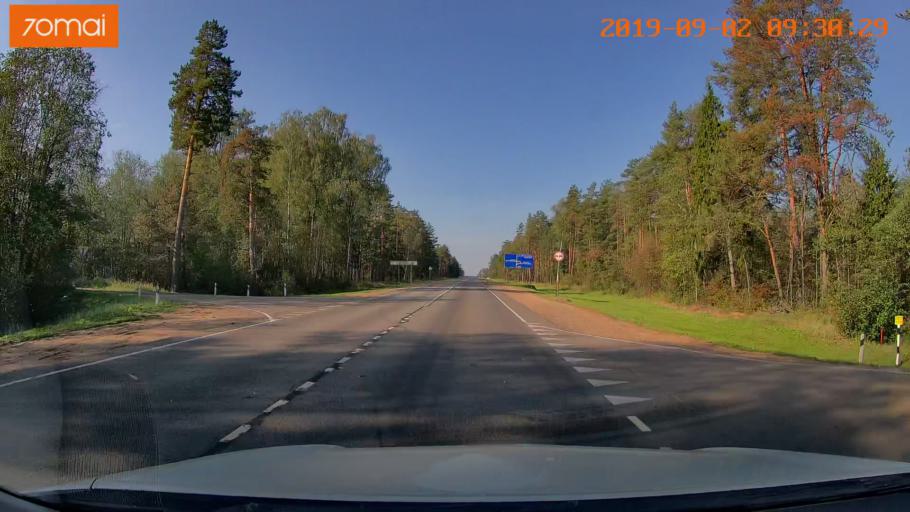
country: RU
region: Kaluga
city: Yukhnov
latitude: 54.7333
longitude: 35.1955
